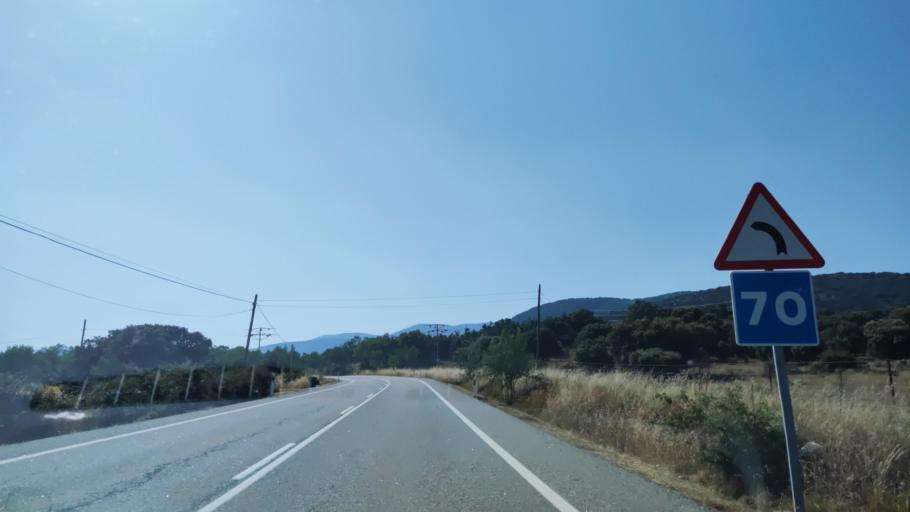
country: ES
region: Madrid
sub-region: Provincia de Madrid
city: Canencia
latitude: 40.9468
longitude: -3.7353
